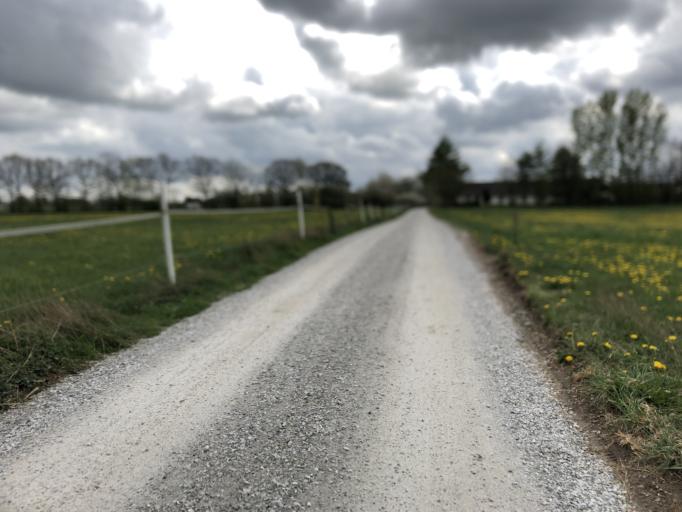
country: SE
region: Skane
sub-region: Eslovs Kommun
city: Eslov
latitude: 55.7319
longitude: 13.2991
